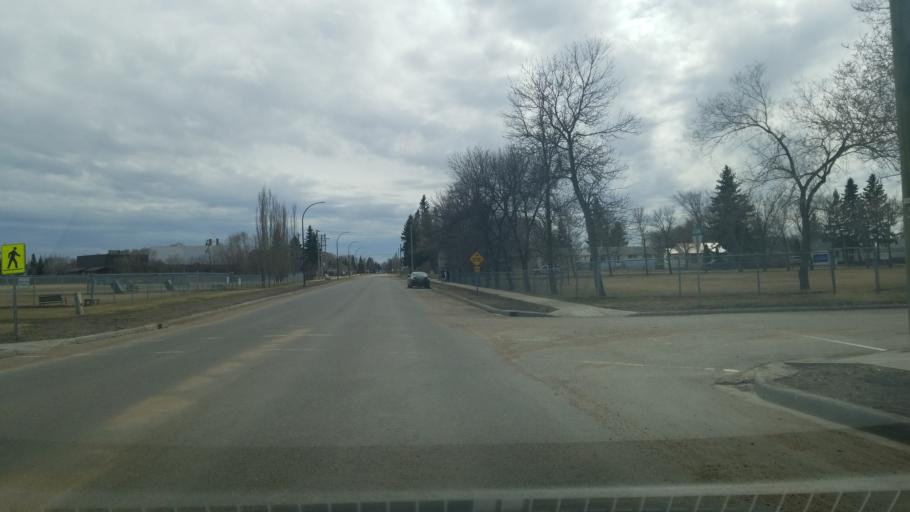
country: CA
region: Saskatchewan
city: Lloydminster
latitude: 53.2762
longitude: -109.9975
